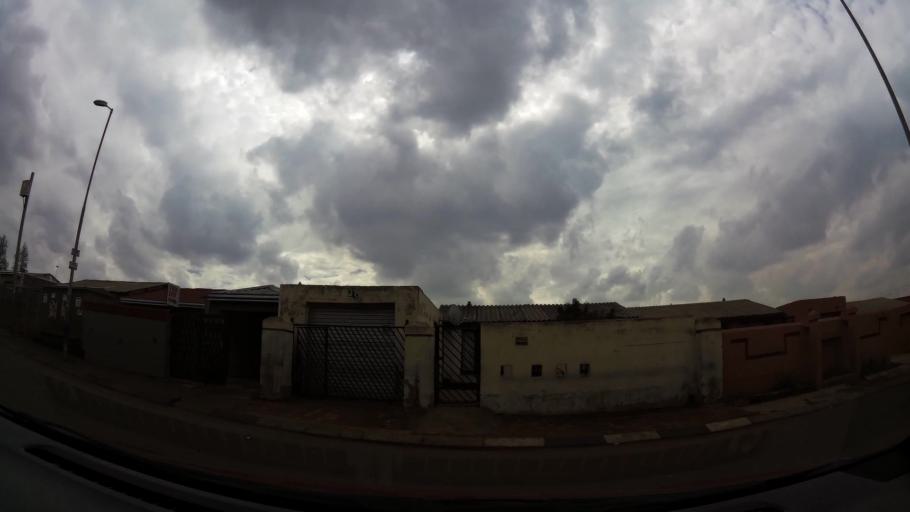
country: ZA
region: Gauteng
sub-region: City of Johannesburg Metropolitan Municipality
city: Soweto
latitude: -26.2579
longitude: 27.8353
